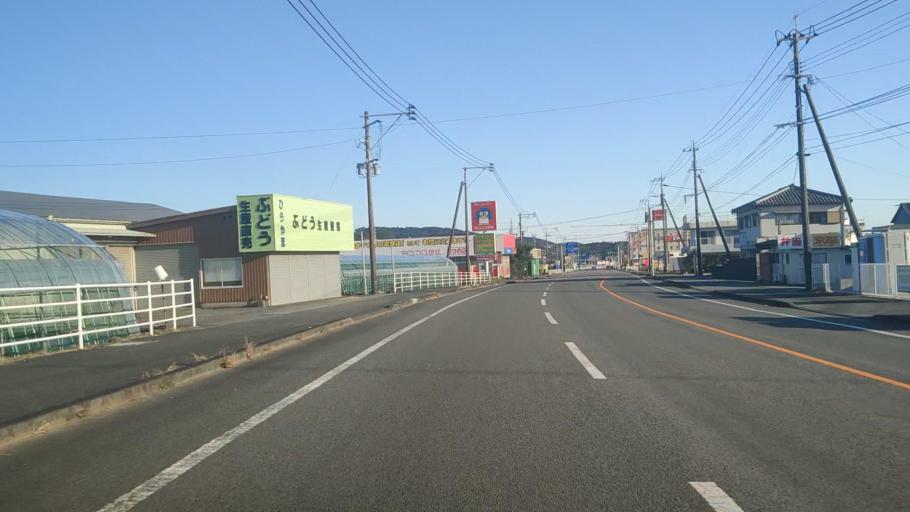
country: JP
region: Miyazaki
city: Takanabe
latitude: 32.2505
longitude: 131.5518
